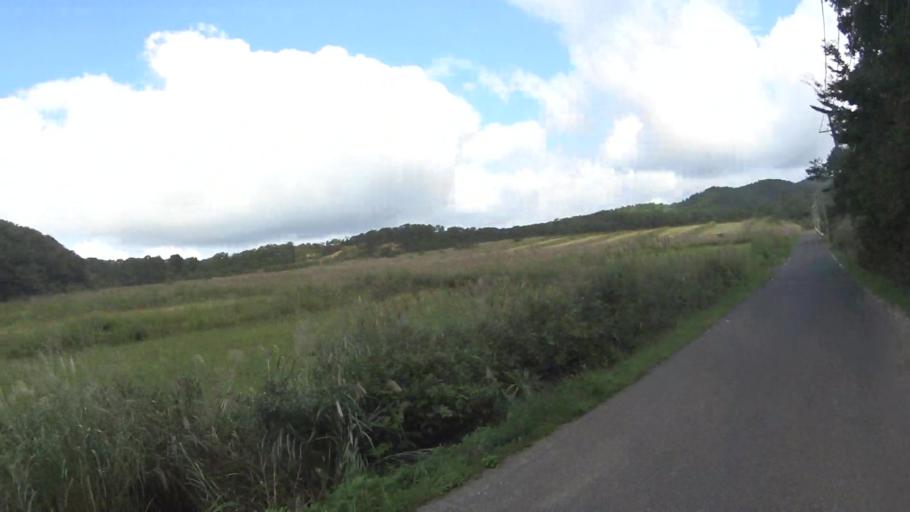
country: JP
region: Kyoto
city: Miyazu
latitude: 35.6521
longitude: 135.1806
